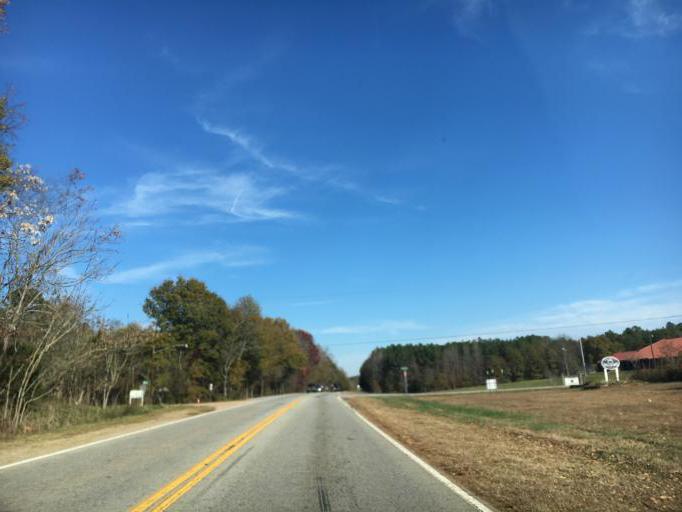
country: US
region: South Carolina
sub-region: Spartanburg County
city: Wellford
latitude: 34.9657
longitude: -82.1107
